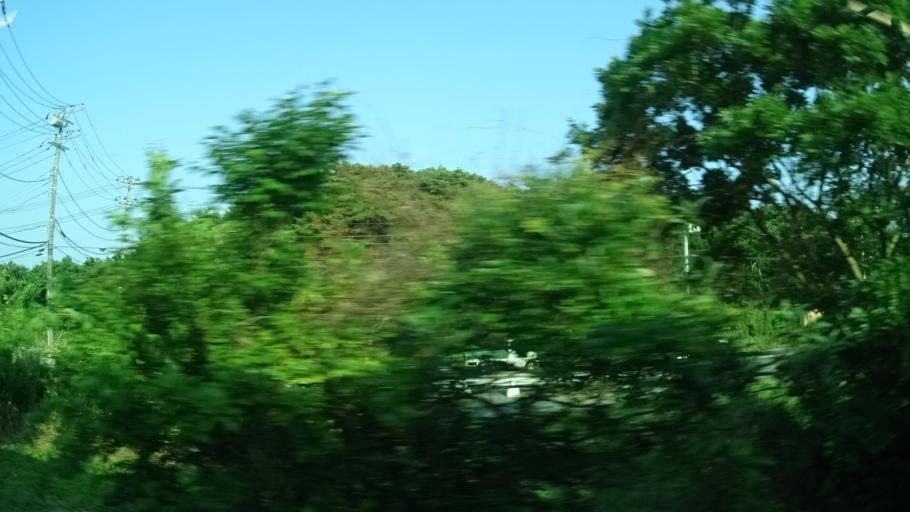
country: JP
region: Ibaraki
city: Takahagi
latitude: 36.6950
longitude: 140.7146
